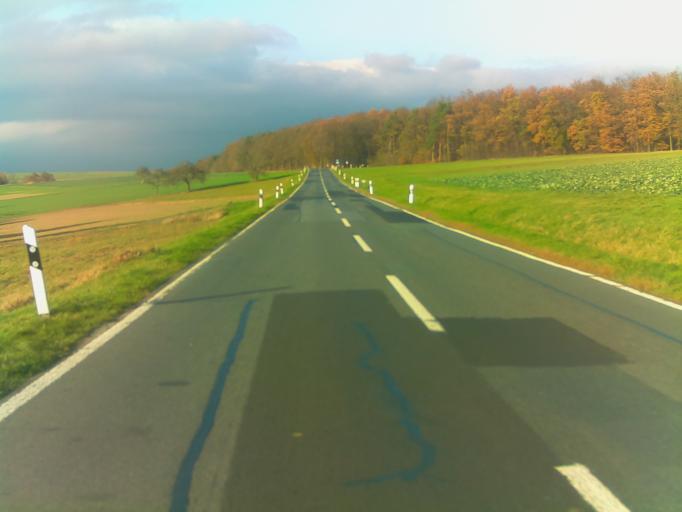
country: DE
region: Bavaria
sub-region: Regierungsbezirk Unterfranken
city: Eichenbuhl
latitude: 49.6929
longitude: 9.3588
